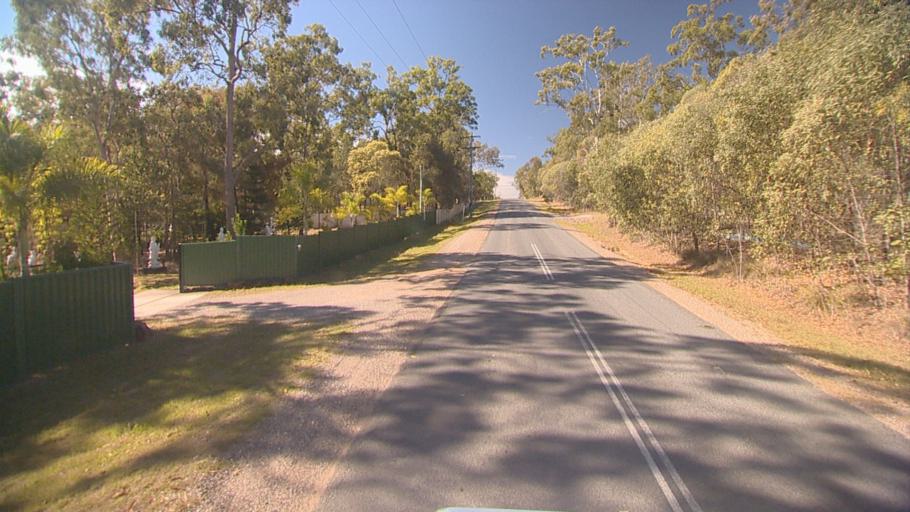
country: AU
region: Queensland
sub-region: Ipswich
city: Springfield Lakes
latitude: -27.7037
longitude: 152.9362
